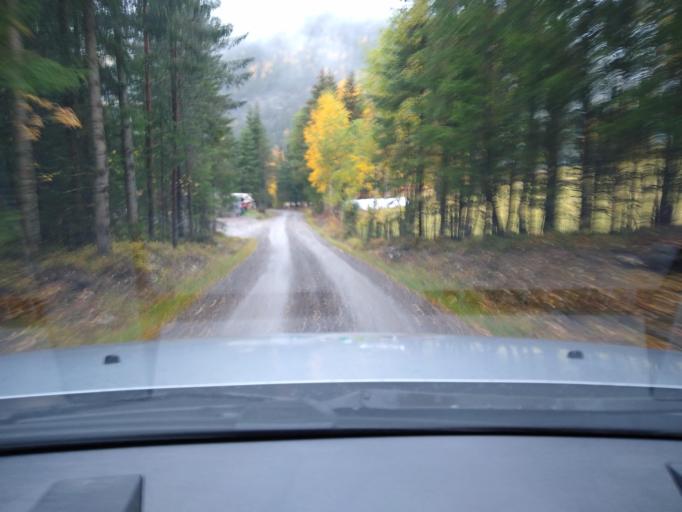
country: NO
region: Oppland
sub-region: Ringebu
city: Ringebu
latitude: 61.5525
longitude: 10.1533
